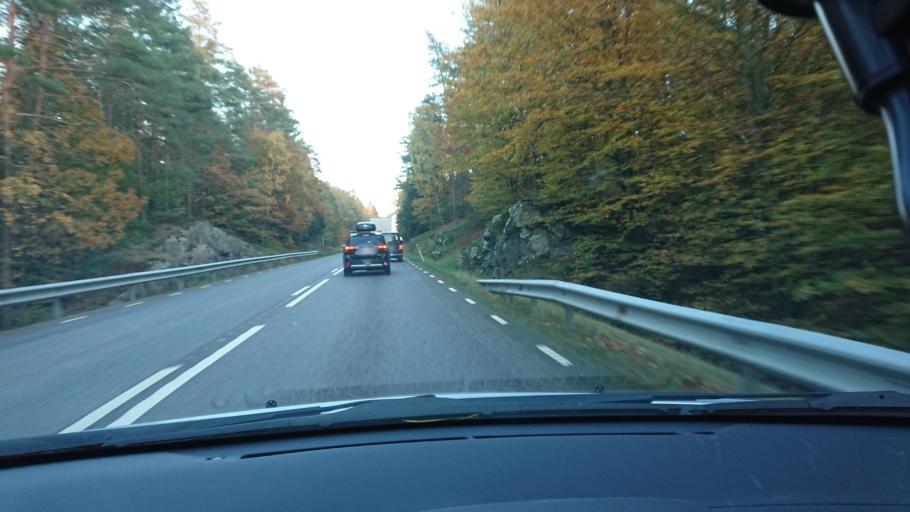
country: SE
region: Halland
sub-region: Laholms Kommun
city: Veinge
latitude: 56.7196
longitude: 13.1764
